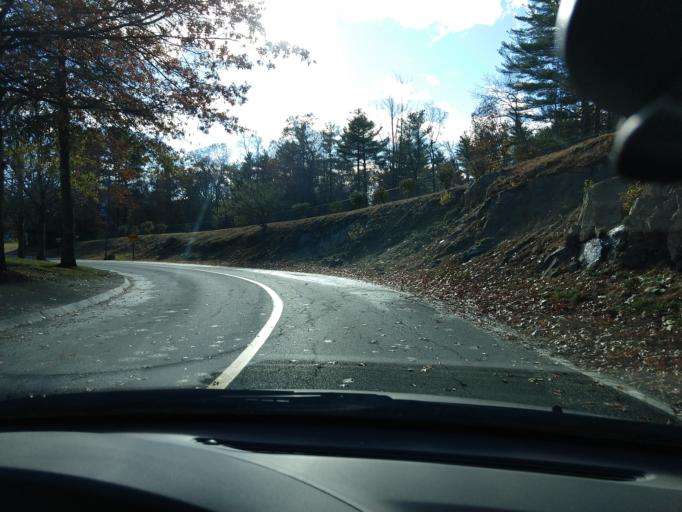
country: US
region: Massachusetts
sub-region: Middlesex County
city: Billerica
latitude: 42.5251
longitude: -71.2754
